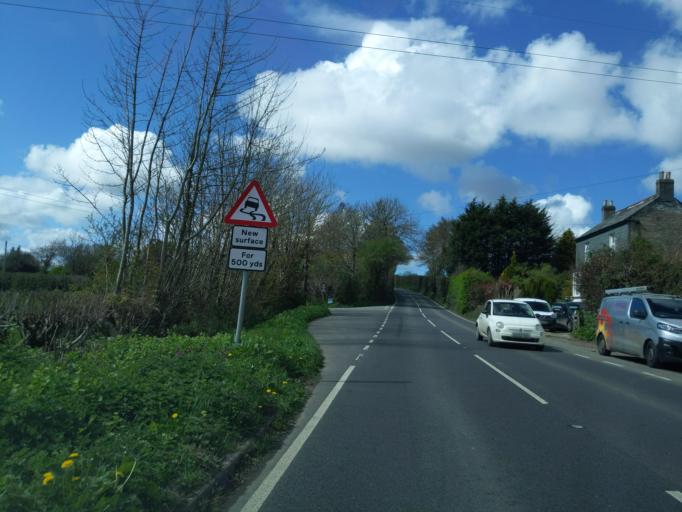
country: GB
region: England
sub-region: Cornwall
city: Bodmin
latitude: 50.4908
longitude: -4.7642
